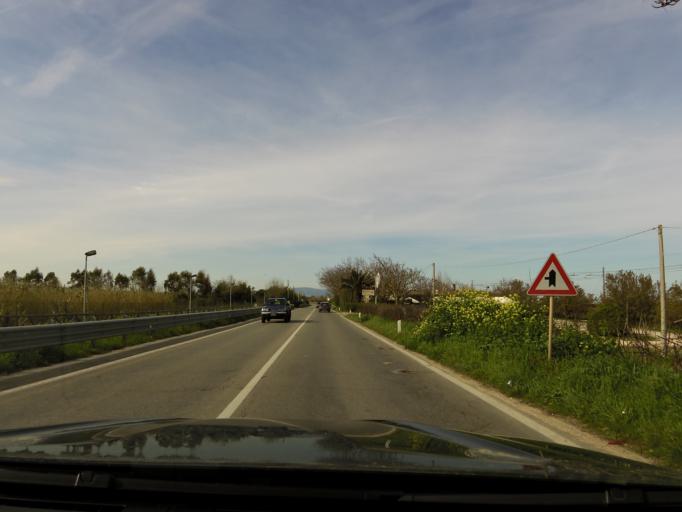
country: IT
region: The Marches
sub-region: Provincia di Macerata
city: Porto Potenza Picena
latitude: 43.3854
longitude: 13.6861
